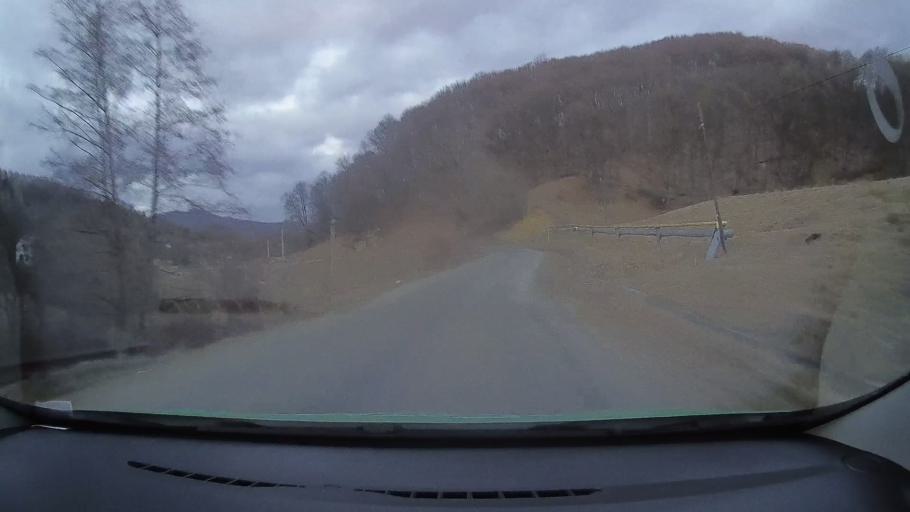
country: RO
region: Dambovita
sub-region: Comuna Visinesti
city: Visinesti
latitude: 45.0967
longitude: 25.5785
